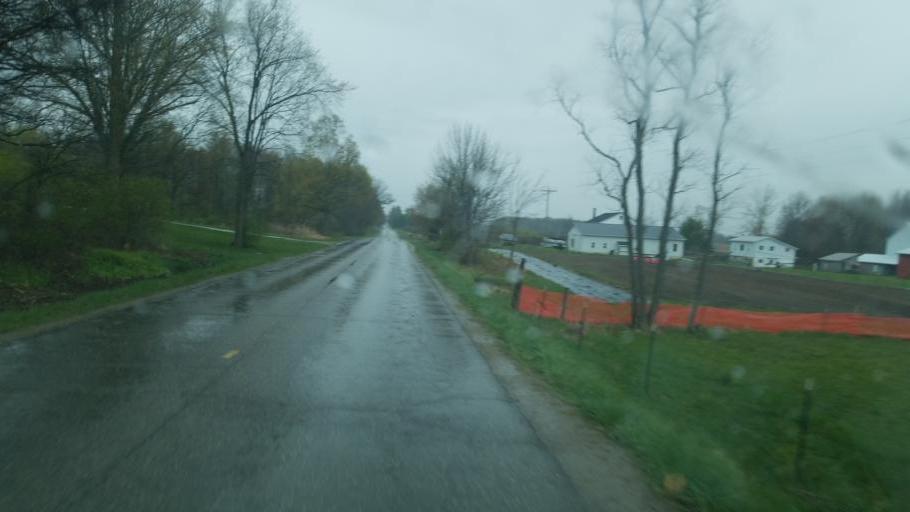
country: US
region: Michigan
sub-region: Montcalm County
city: Lakeview
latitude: 43.5062
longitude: -85.2842
